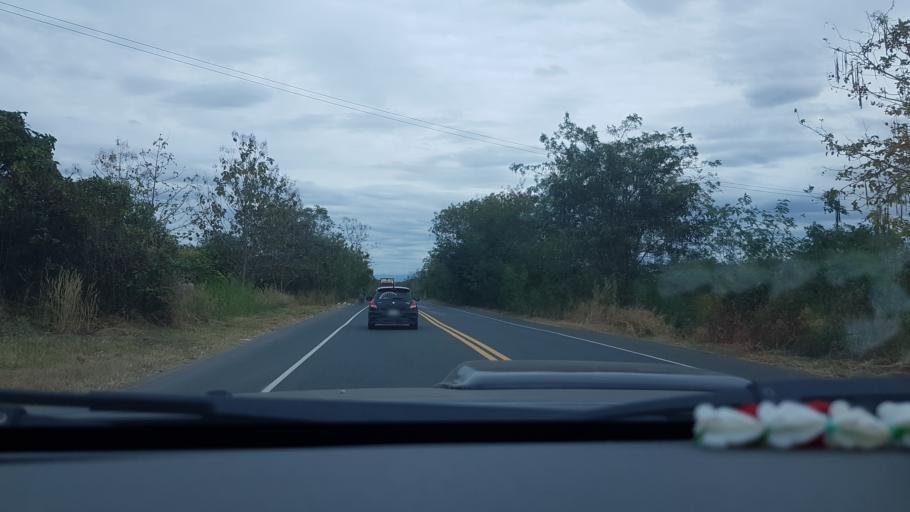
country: TH
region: Phetchabun
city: Phetchabun
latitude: 16.4737
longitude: 101.1298
